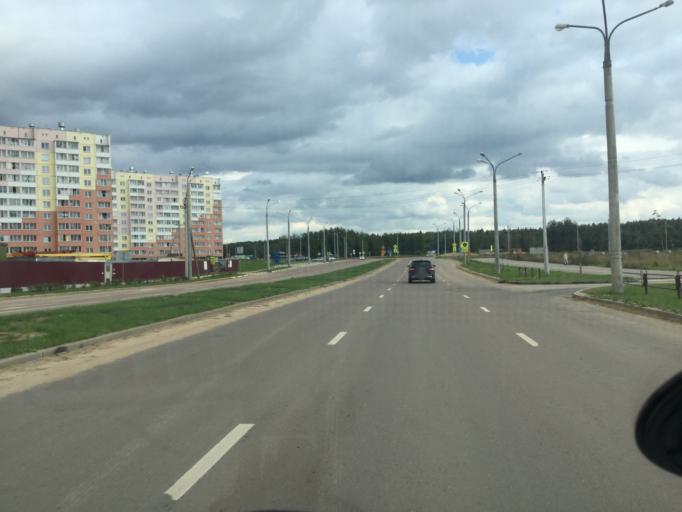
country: BY
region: Vitebsk
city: Vitebsk
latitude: 55.1637
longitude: 30.2765
